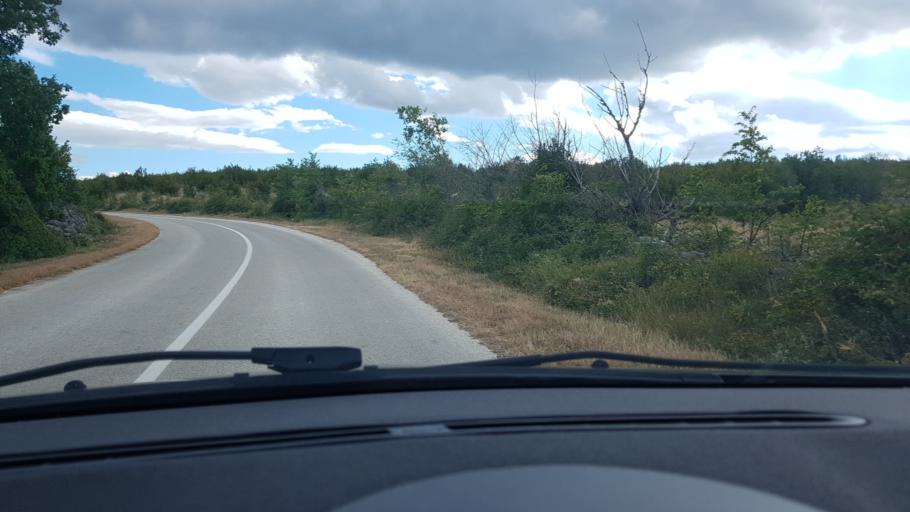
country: HR
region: Sibensko-Kniniska
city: Kistanje
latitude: 44.0990
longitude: 15.9369
